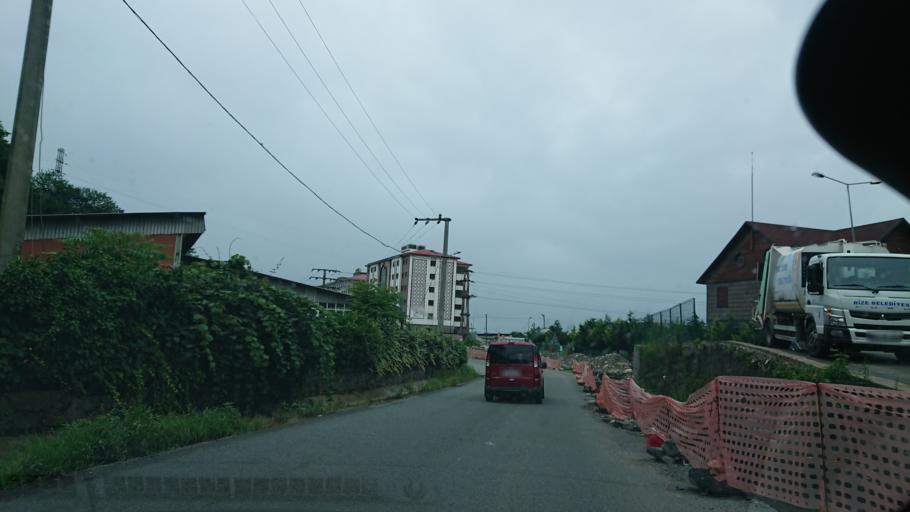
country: TR
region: Rize
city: Gundogdu
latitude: 41.0374
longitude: 40.5789
